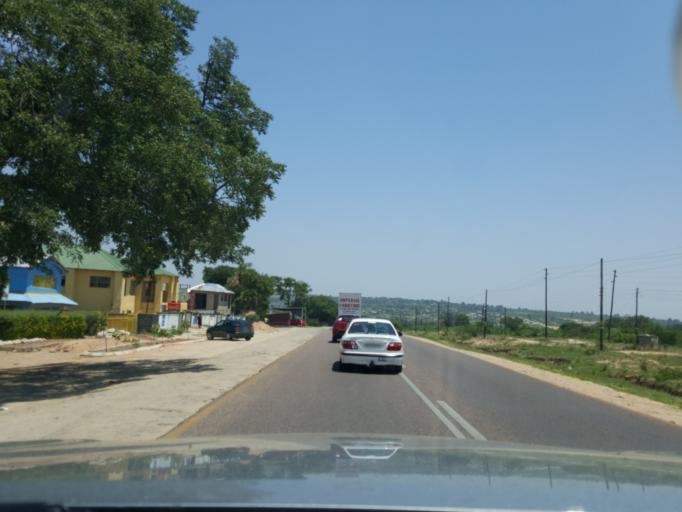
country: ZA
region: Limpopo
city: Thulamahashi
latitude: -24.7977
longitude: 31.0831
